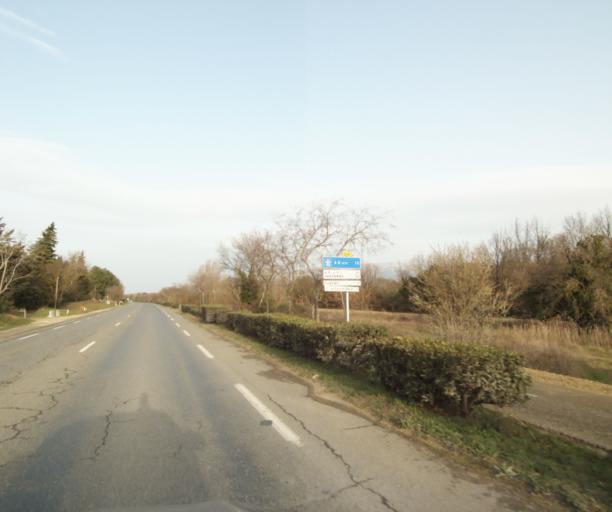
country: FR
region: Provence-Alpes-Cote d'Azur
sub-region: Departement des Bouches-du-Rhone
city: Trets
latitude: 43.4538
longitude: 5.6681
